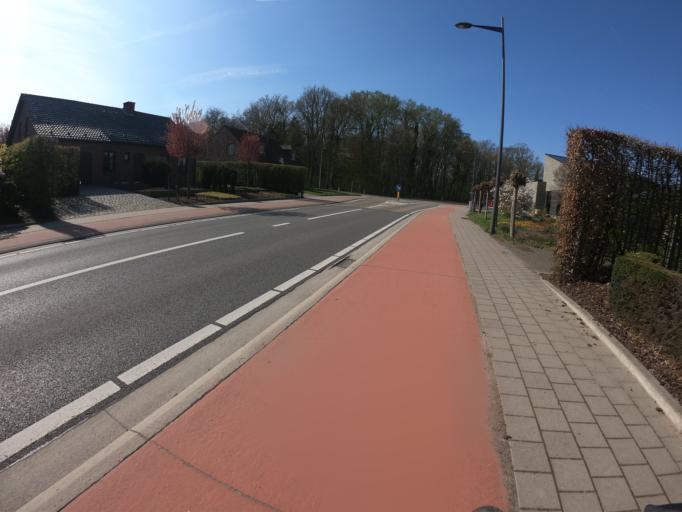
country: BE
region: Flanders
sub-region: Provincie Limburg
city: Herk-de-Stad
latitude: 50.9374
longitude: 5.1703
